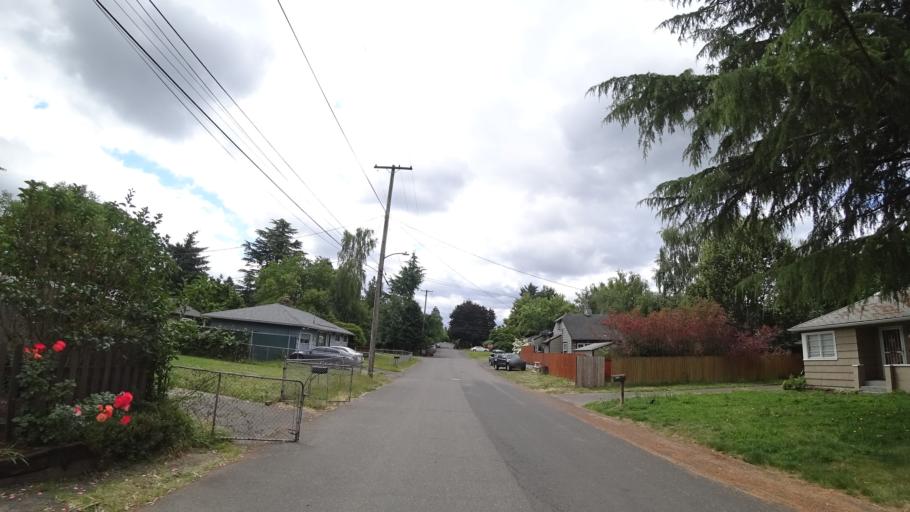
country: US
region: Oregon
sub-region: Multnomah County
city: Portland
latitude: 45.5670
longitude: -122.6091
